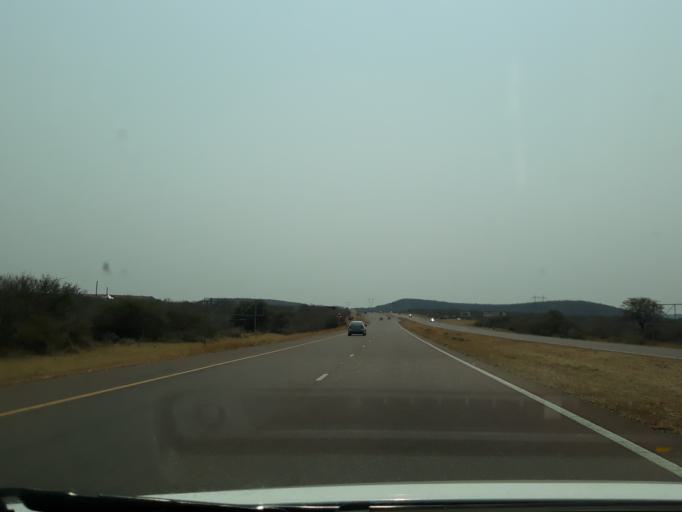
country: BW
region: Kgatleng
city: Bokaa
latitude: -24.4061
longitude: 26.0540
